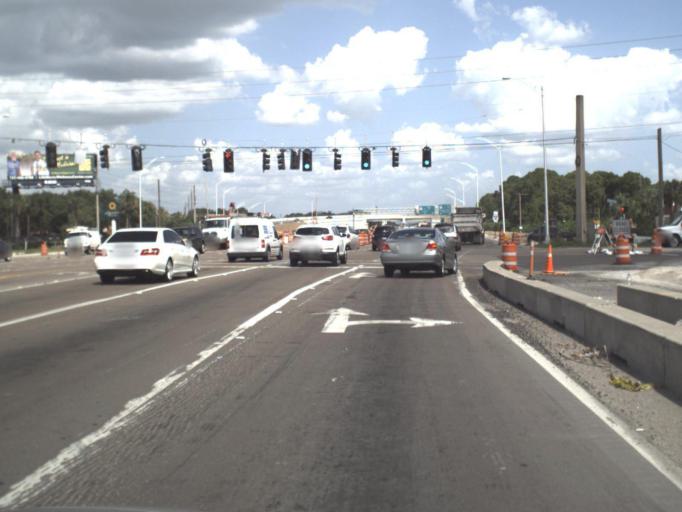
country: US
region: Florida
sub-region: Pinellas County
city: Feather Sound
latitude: 27.8937
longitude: -82.6801
